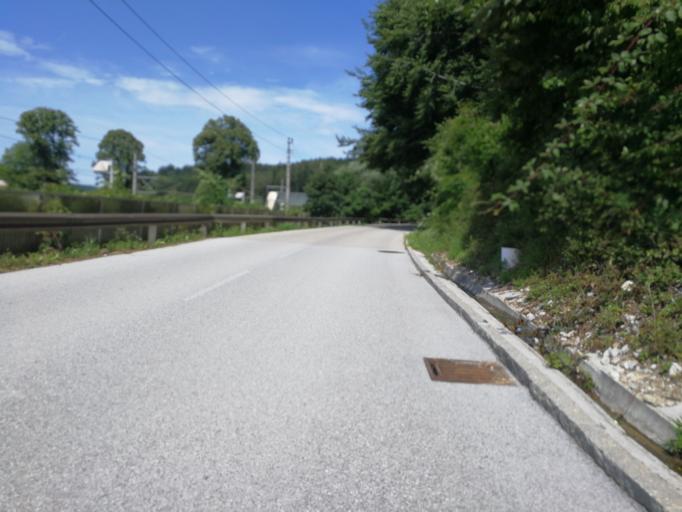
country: AT
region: Salzburg
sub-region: Politischer Bezirk Salzburg-Umgebung
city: Hallwang
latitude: 47.8381
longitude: 13.0658
